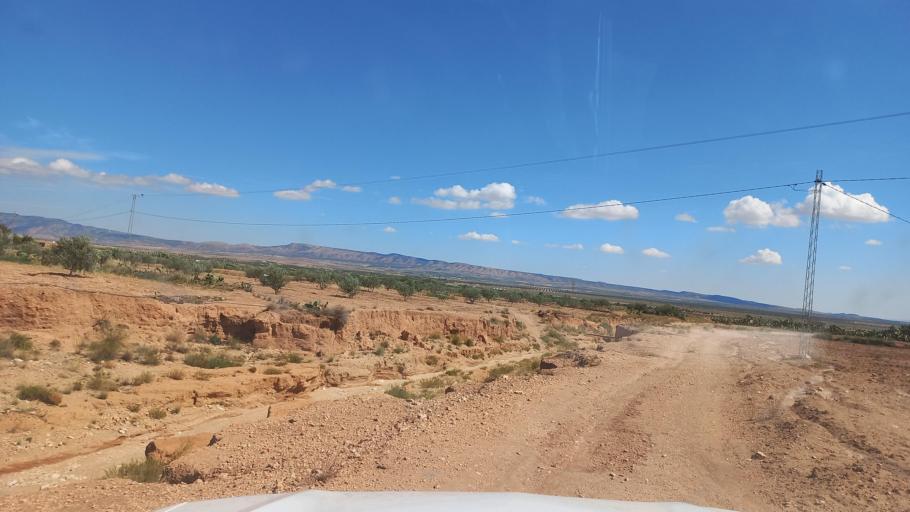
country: TN
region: Al Qasrayn
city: Sbiba
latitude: 35.3556
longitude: 9.0149
